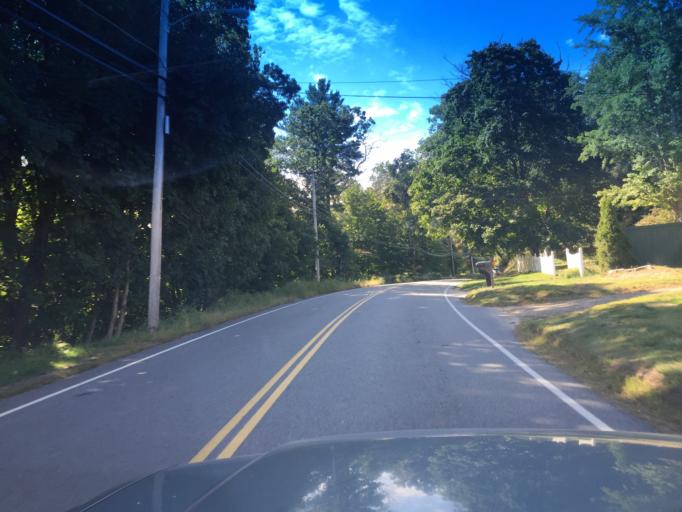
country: US
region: Massachusetts
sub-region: Worcester County
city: Northborough
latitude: 42.3349
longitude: -71.6267
